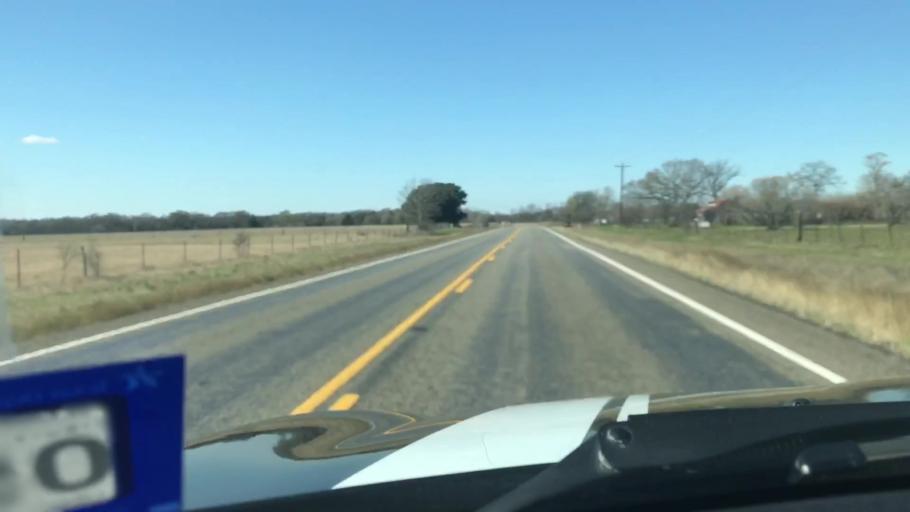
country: US
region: Texas
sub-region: Robertson County
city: Calvert
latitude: 30.8867
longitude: -96.8063
